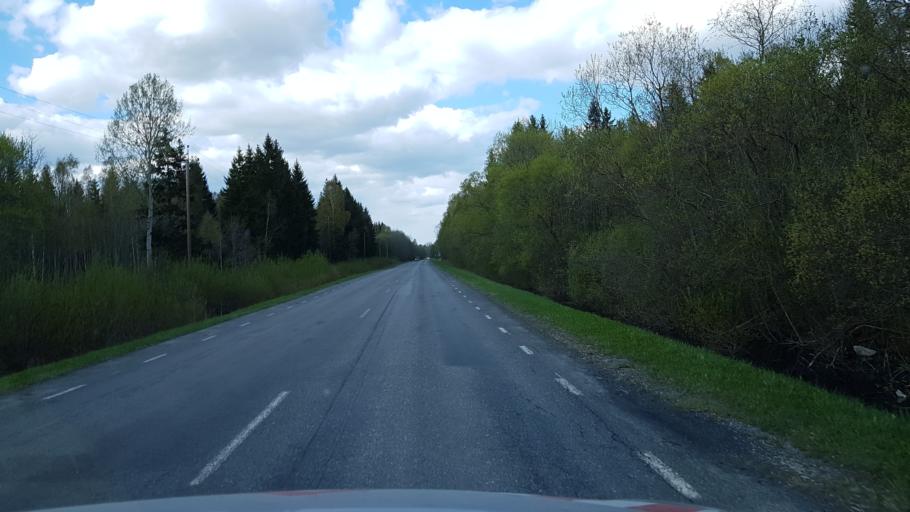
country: EE
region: Harju
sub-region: Keila linn
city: Keila
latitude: 59.2587
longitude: 24.4546
